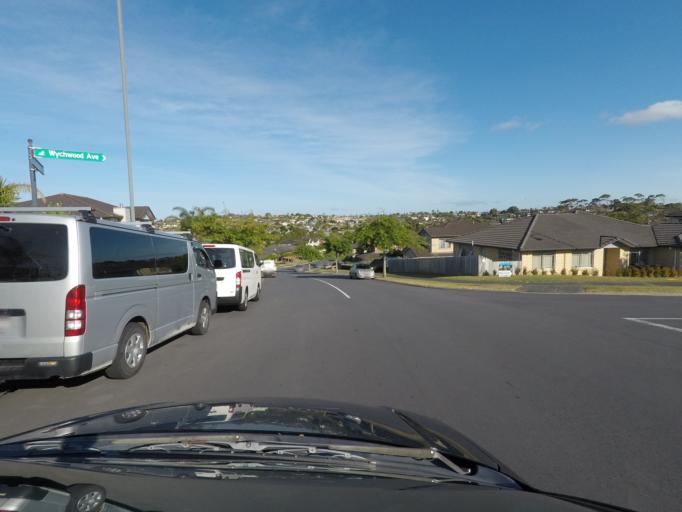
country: NZ
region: Auckland
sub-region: Auckland
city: Waitakere
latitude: -36.8817
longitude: 174.6027
